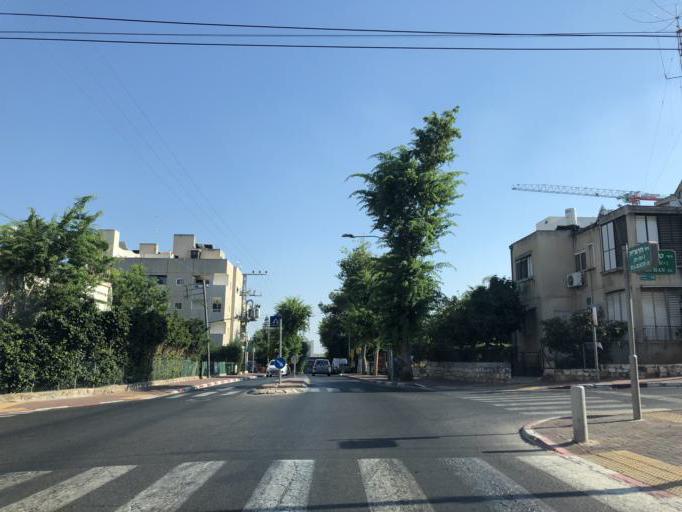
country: IL
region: Tel Aviv
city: Giv`atayim
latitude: 32.0685
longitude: 34.8244
